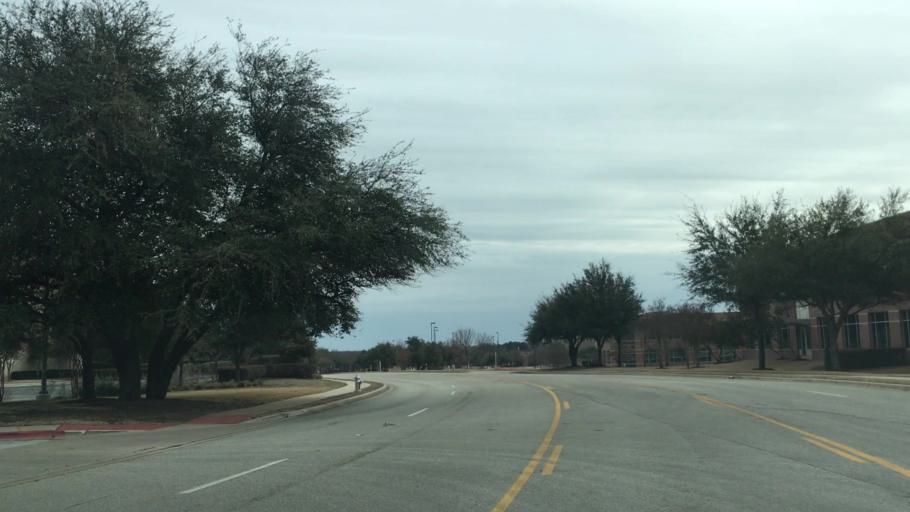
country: US
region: Texas
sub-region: Williamson County
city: Jollyville
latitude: 30.4729
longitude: -97.7753
